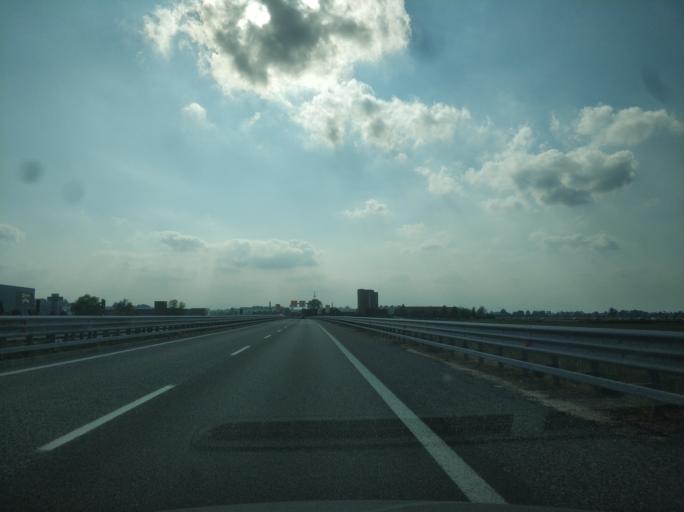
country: IT
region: Piedmont
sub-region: Provincia di Cuneo
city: Cervere
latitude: 44.6635
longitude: 7.7861
